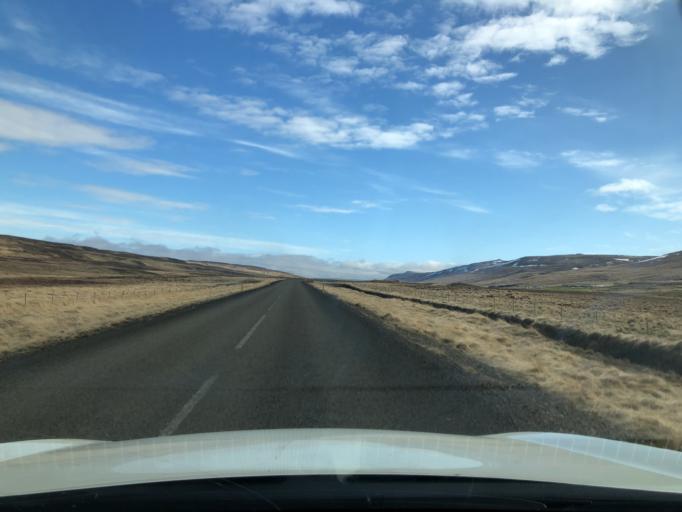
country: IS
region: West
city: Borgarnes
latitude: 65.1219
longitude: -21.6647
